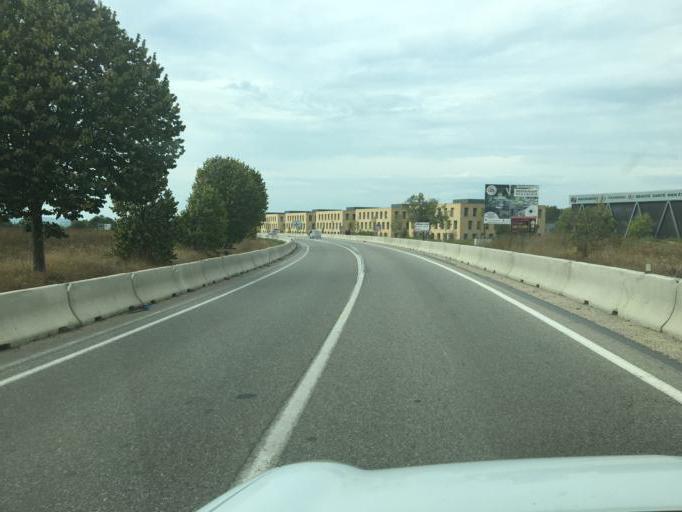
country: FR
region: Provence-Alpes-Cote d'Azur
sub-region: Departement des Bouches-du-Rhone
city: Bouc-Bel-Air
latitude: 43.4776
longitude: 5.3970
